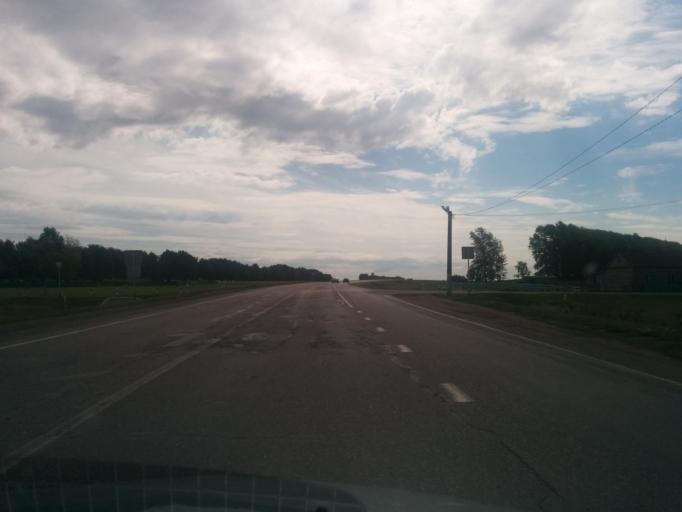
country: RU
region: Bashkortostan
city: Kabakovo
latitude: 54.4654
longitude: 55.9579
